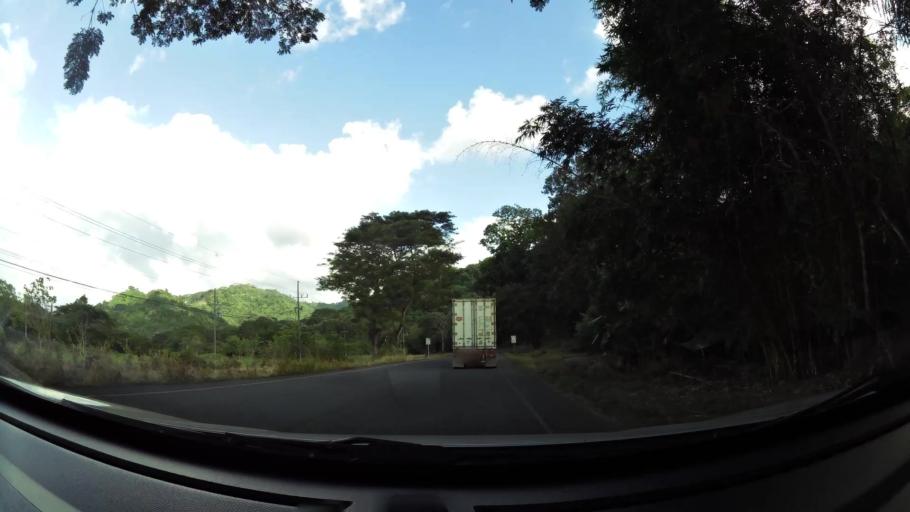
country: CR
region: Puntarenas
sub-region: Canton de Garabito
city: Jaco
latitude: 9.7551
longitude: -84.6213
